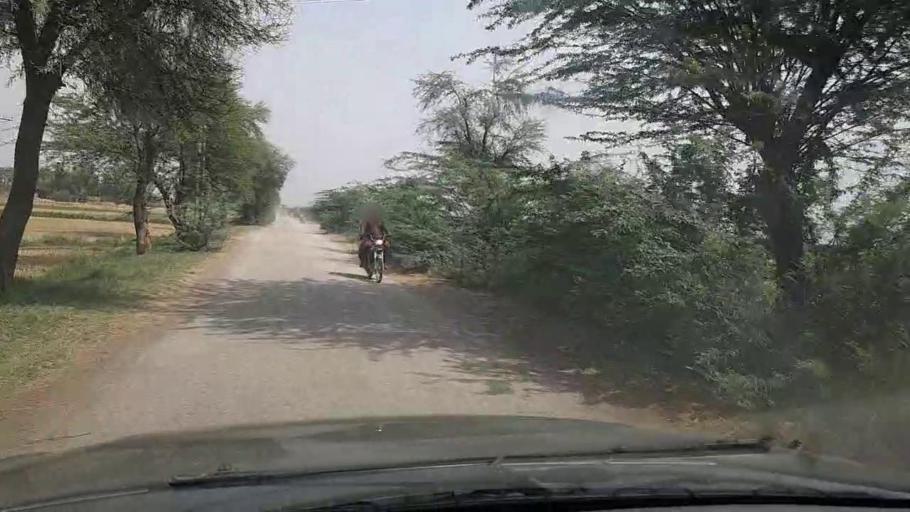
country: PK
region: Sindh
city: Shikarpur
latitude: 27.9189
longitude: 68.6810
